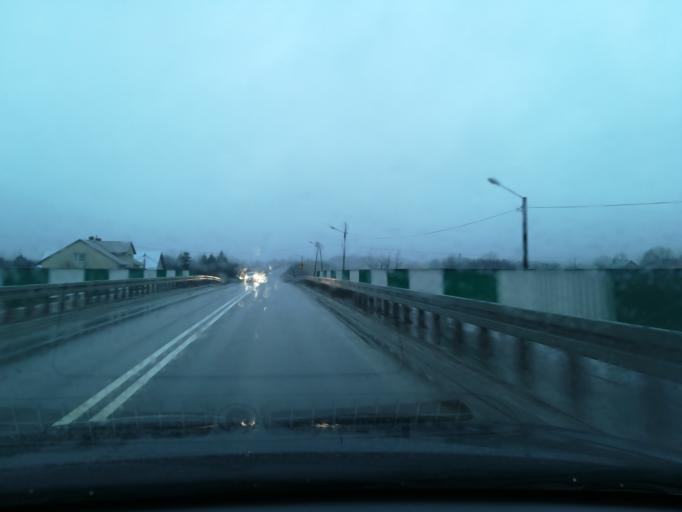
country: PL
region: Subcarpathian Voivodeship
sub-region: Powiat lancucki
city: Bialobrzegi
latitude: 50.1118
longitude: 22.3362
